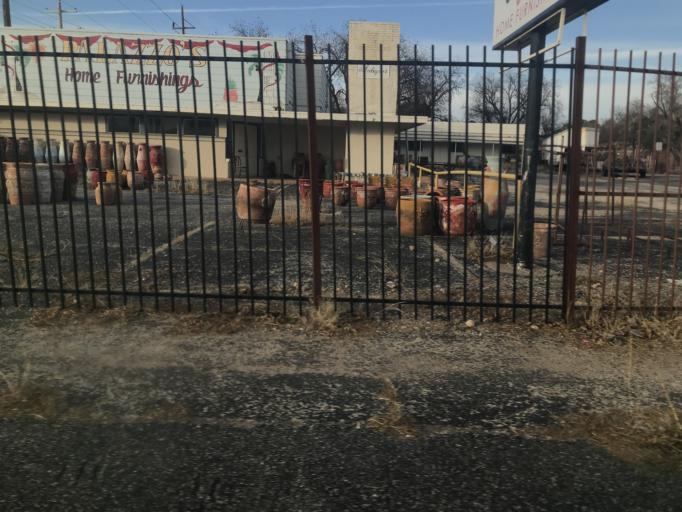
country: US
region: Texas
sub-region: Taylor County
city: Abilene
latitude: 32.4323
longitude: -99.7529
